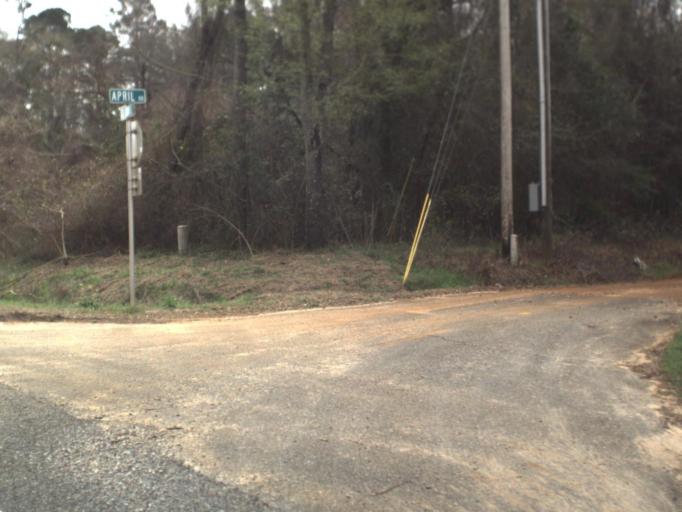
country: US
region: Florida
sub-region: Leon County
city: Tallahassee
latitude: 30.4245
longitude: -84.1769
